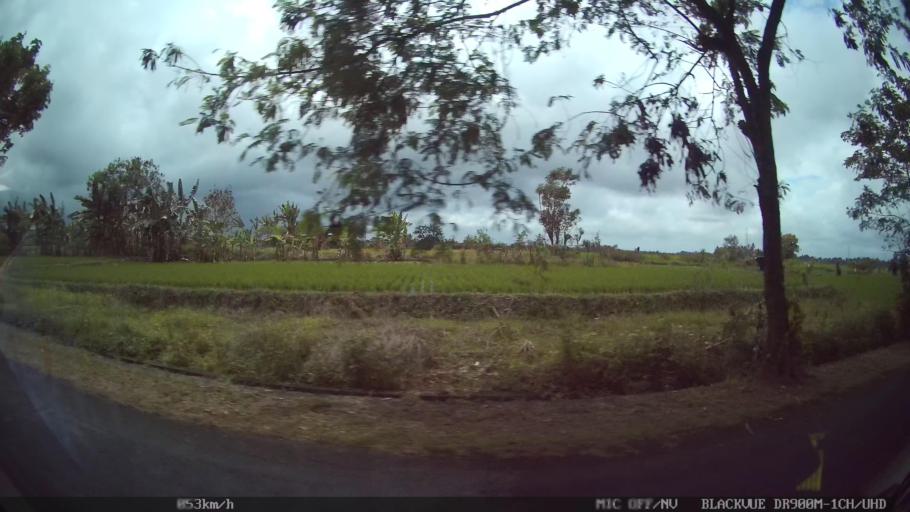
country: ID
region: Bali
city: Banjar Serangan
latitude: -8.5313
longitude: 115.1795
